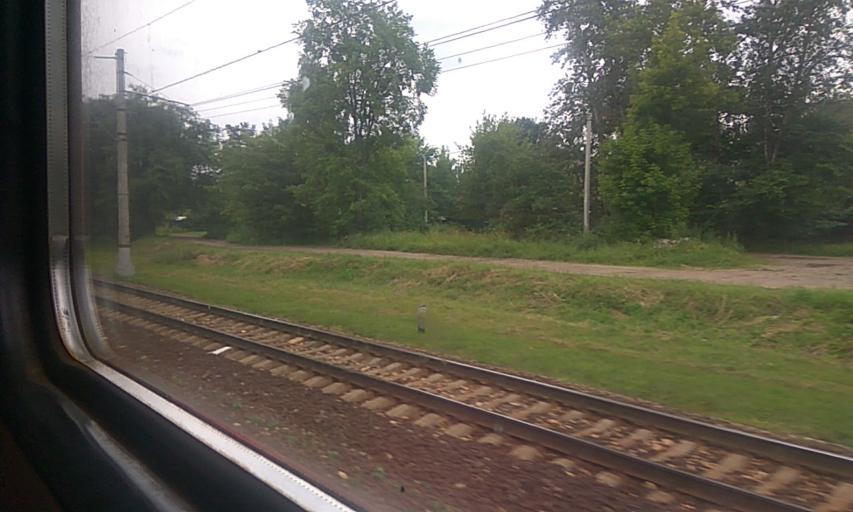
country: RU
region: Moskovskaya
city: Kraskovo
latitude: 55.6488
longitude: 37.9889
